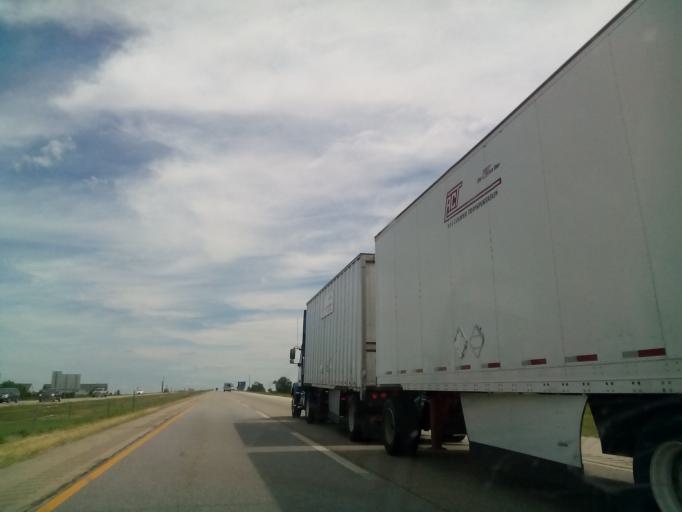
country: US
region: Illinois
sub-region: DeKalb County
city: DeKalb
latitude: 41.9037
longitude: -88.7615
